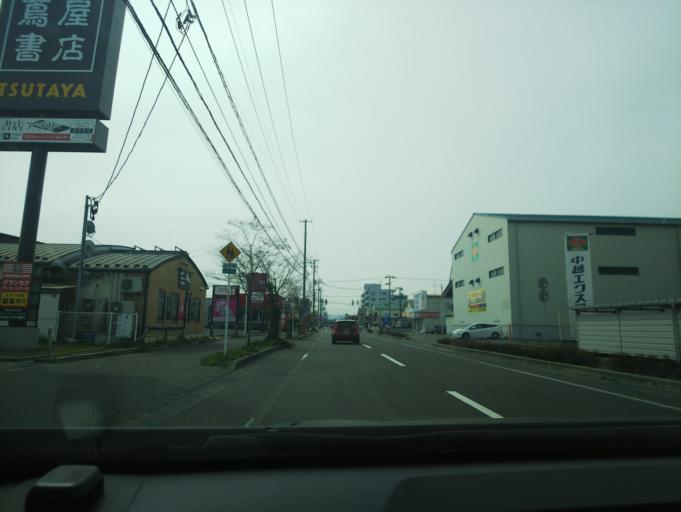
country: JP
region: Niigata
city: Niigata-shi
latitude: 37.9076
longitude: 139.0694
